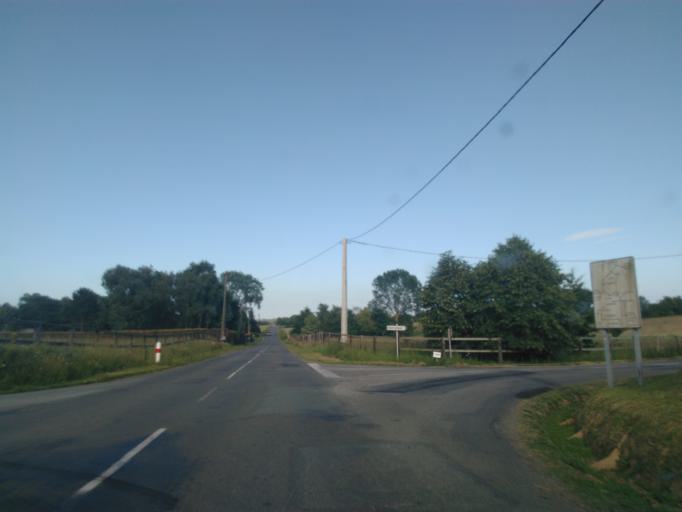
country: FR
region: Brittany
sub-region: Departement d'Ille-et-Vilaine
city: Romille
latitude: 48.2165
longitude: -1.8604
